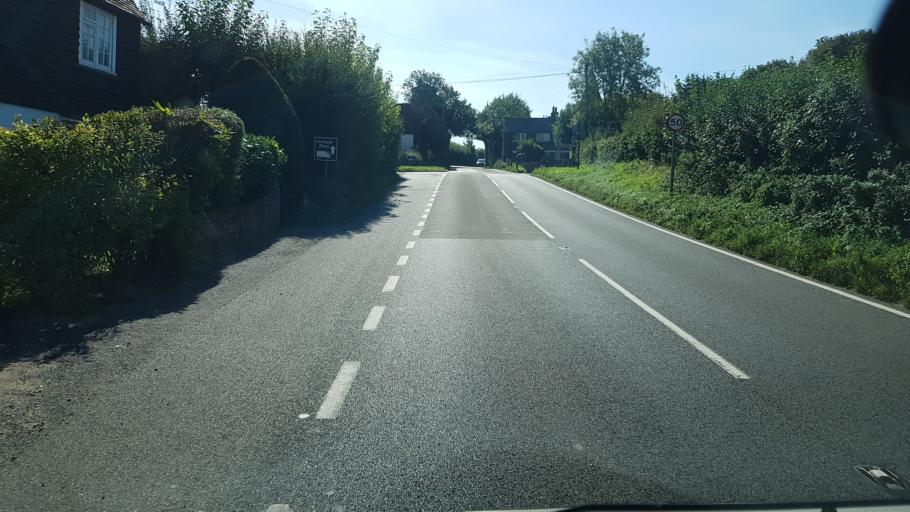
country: GB
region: England
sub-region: Kent
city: Borough Green
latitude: 51.2887
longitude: 0.3496
